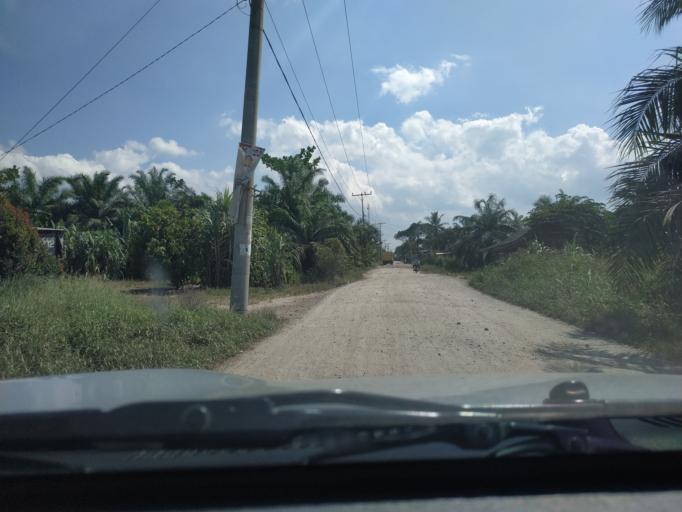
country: ID
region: North Sumatra
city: Tanjungbalai
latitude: 2.8786
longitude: 99.8615
